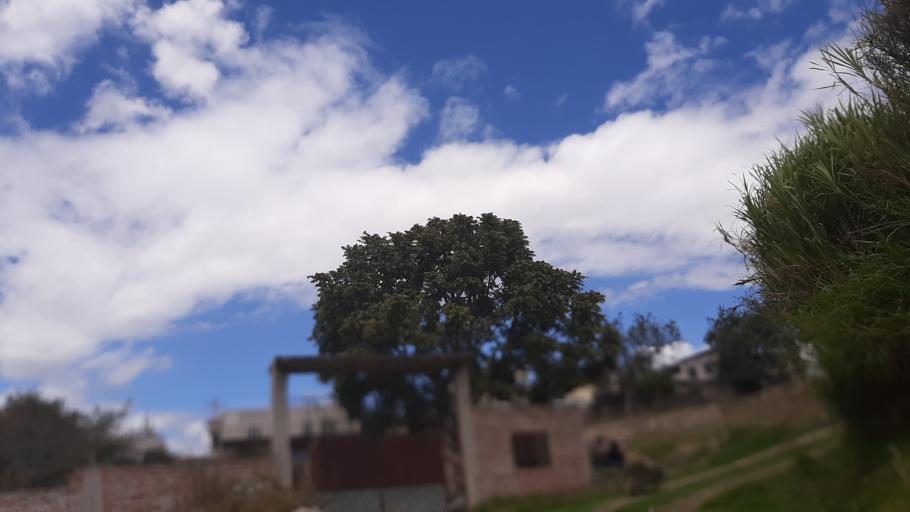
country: EC
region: Chimborazo
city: Riobamba
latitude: -1.6575
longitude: -78.6333
